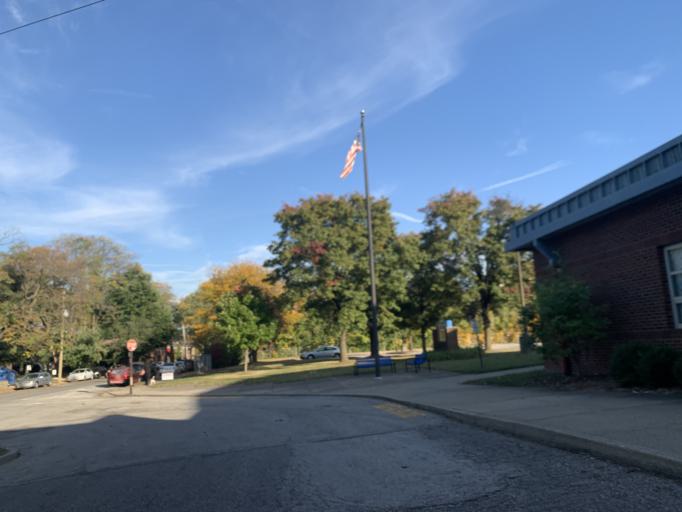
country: US
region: Kentucky
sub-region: Jefferson County
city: Louisville
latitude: 38.2248
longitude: -85.7641
